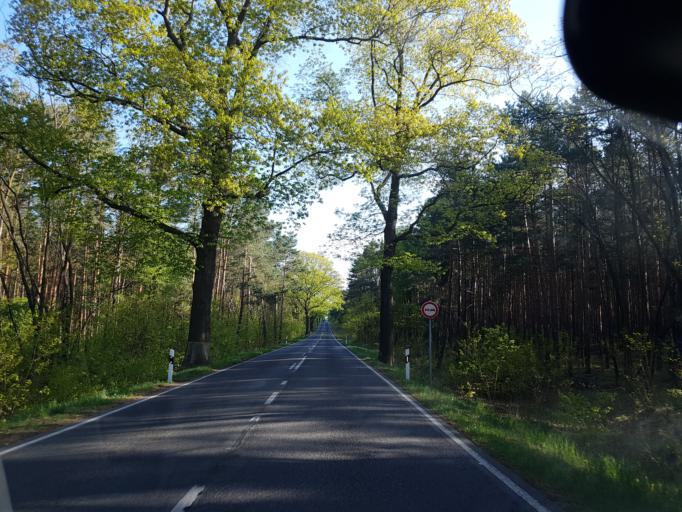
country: DE
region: Brandenburg
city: Altdobern
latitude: 51.6211
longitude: 14.0250
